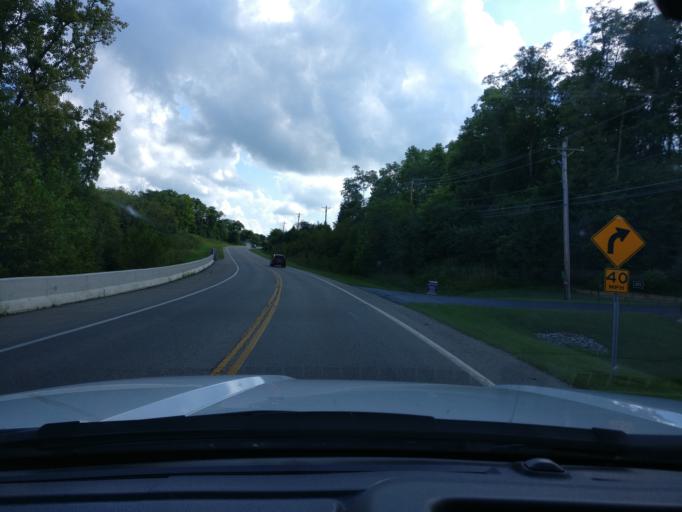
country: US
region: Ohio
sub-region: Warren County
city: Five Points
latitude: 39.5215
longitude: -84.1832
